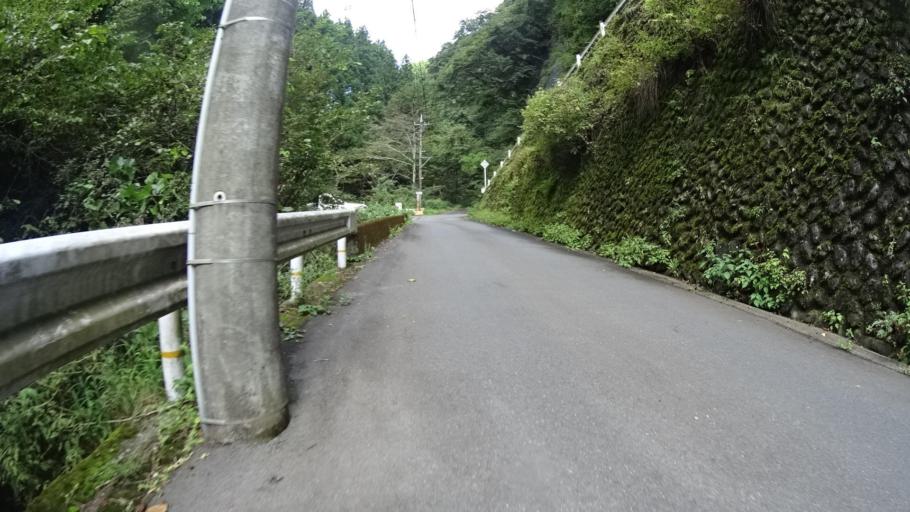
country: JP
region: Yamanashi
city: Uenohara
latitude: 35.7387
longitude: 139.0618
